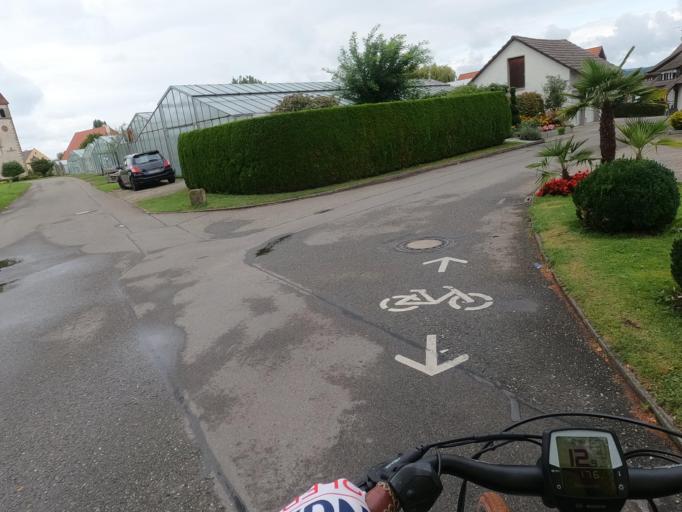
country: DE
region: Baden-Wuerttemberg
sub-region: Freiburg Region
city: Reichenau
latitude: 47.7062
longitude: 9.0461
